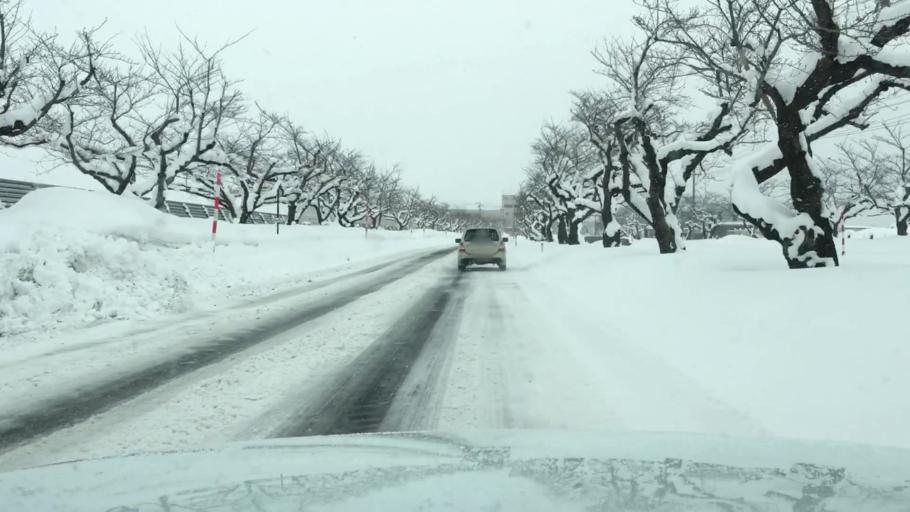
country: JP
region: Aomori
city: Hirosaki
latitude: 40.6380
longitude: 140.4890
